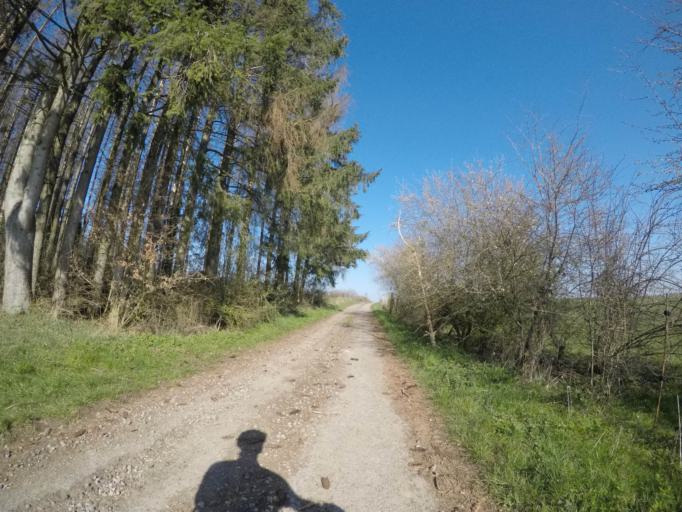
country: BE
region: Wallonia
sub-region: Province du Luxembourg
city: Etalle
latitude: 49.7117
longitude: 5.5748
